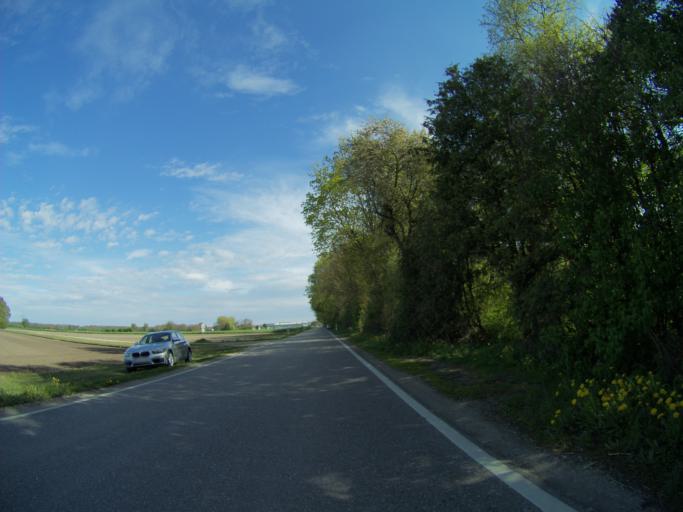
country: DE
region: Bavaria
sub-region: Upper Bavaria
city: Freising
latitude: 48.3754
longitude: 11.6998
